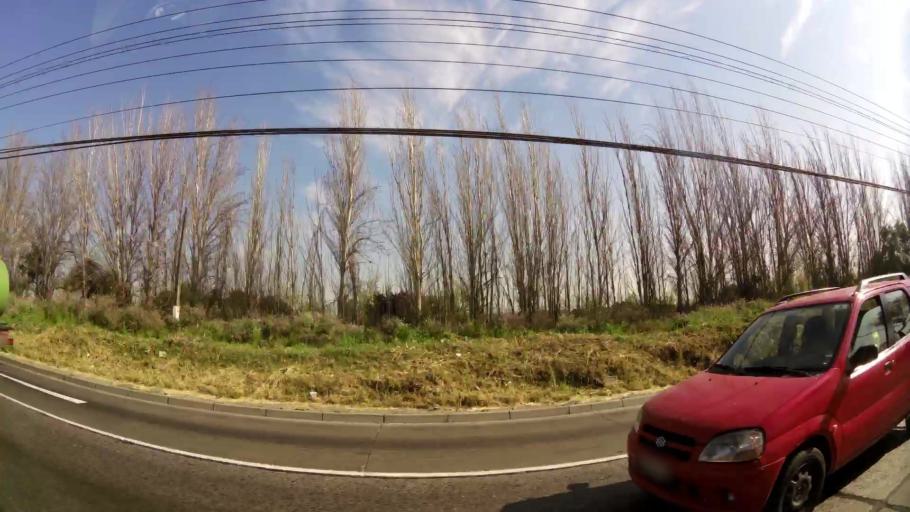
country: CL
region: Santiago Metropolitan
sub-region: Provincia de Maipo
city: San Bernardo
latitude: -33.5394
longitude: -70.7747
